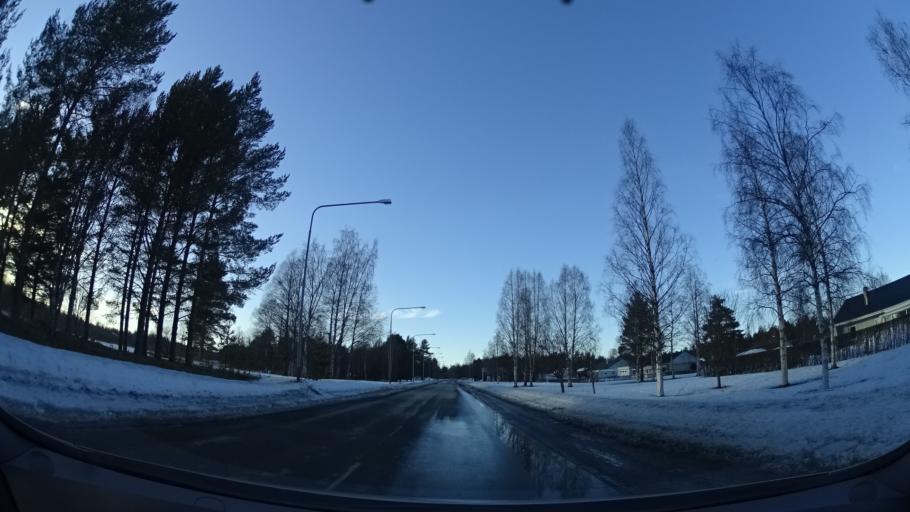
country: SE
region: Vaesterbotten
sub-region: Skelleftea Kommun
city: Byske
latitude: 64.9476
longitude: 21.2258
